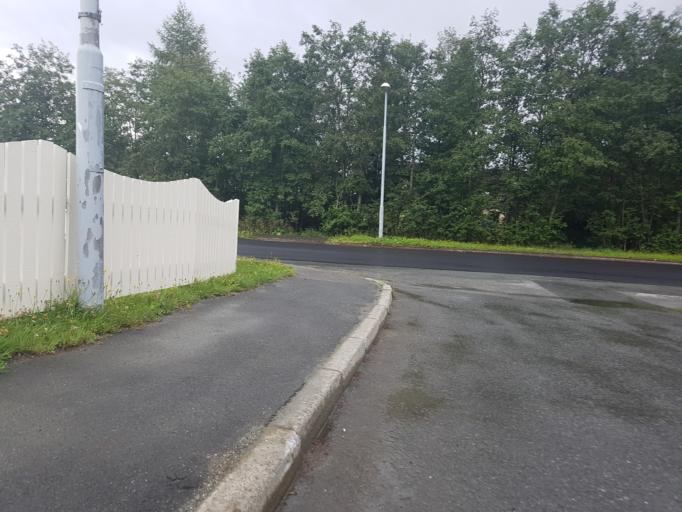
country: NO
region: Sor-Trondelag
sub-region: Trondheim
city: Trondheim
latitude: 63.3885
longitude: 10.3551
